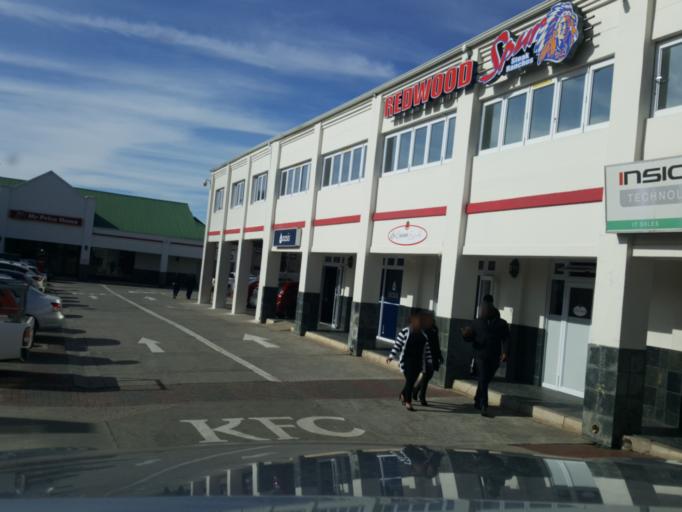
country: ZA
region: Eastern Cape
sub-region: Cacadu District Municipality
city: Grahamstown
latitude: -33.3101
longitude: 26.5218
